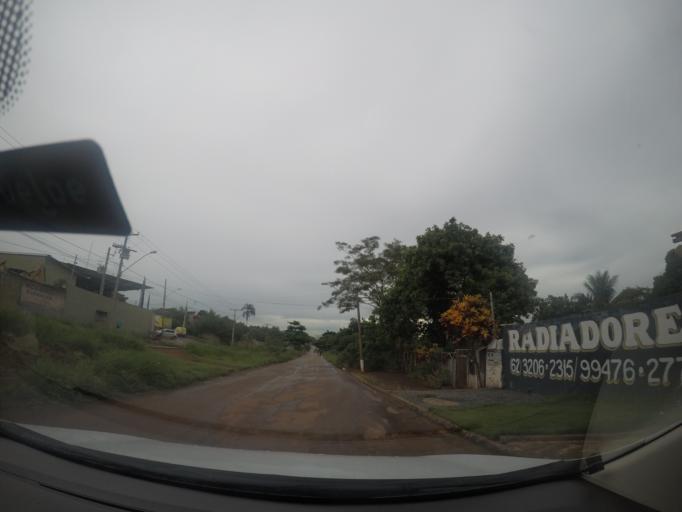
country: BR
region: Goias
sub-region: Goiania
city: Goiania
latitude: -16.6258
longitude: -49.2351
